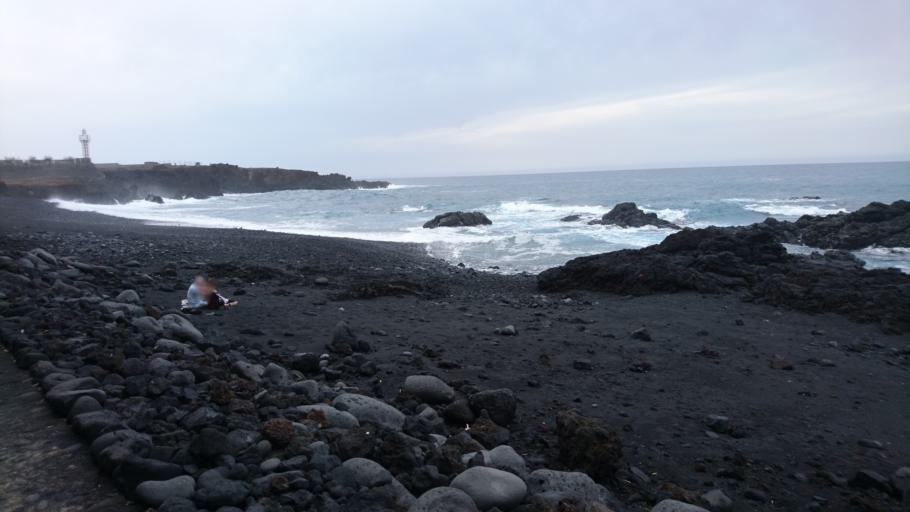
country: ES
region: Canary Islands
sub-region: Provincia de Santa Cruz de Tenerife
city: Tazacorte
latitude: 28.6022
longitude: -17.9234
